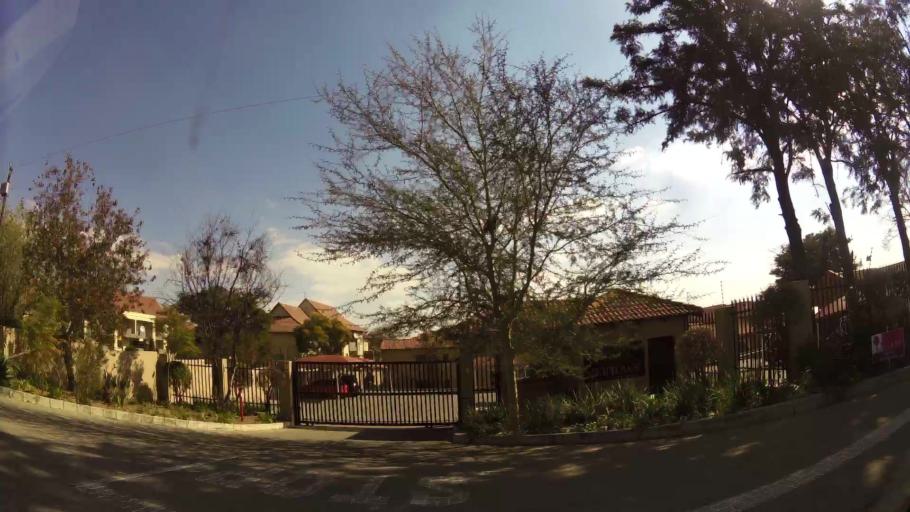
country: ZA
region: Gauteng
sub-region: City of Johannesburg Metropolitan Municipality
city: Midrand
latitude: -26.0057
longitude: 28.1140
